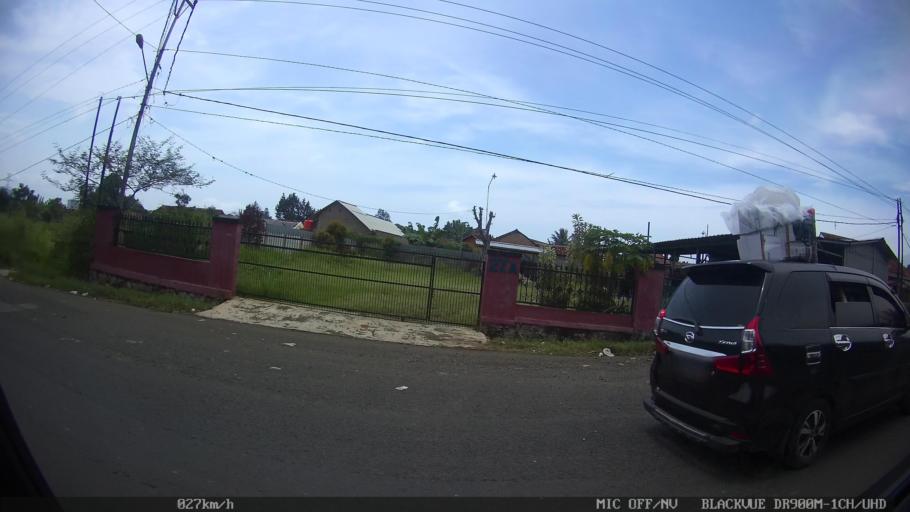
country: ID
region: Lampung
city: Bandarlampung
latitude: -5.4385
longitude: 105.2409
